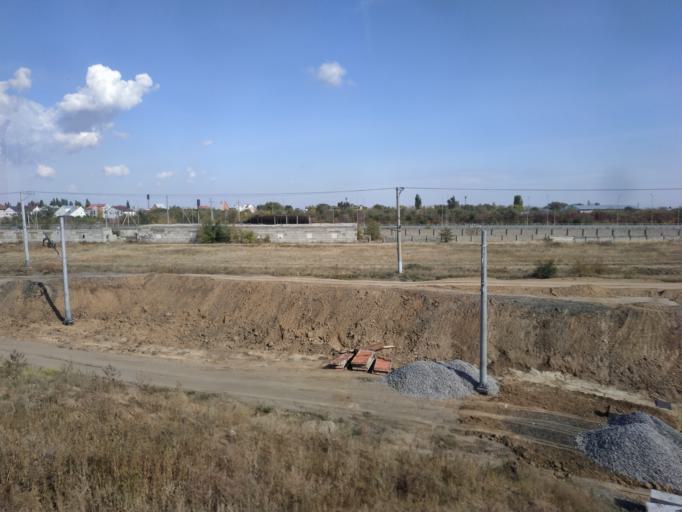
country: RU
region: Volgograd
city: Gumrak
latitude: 48.7709
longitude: 44.3905
